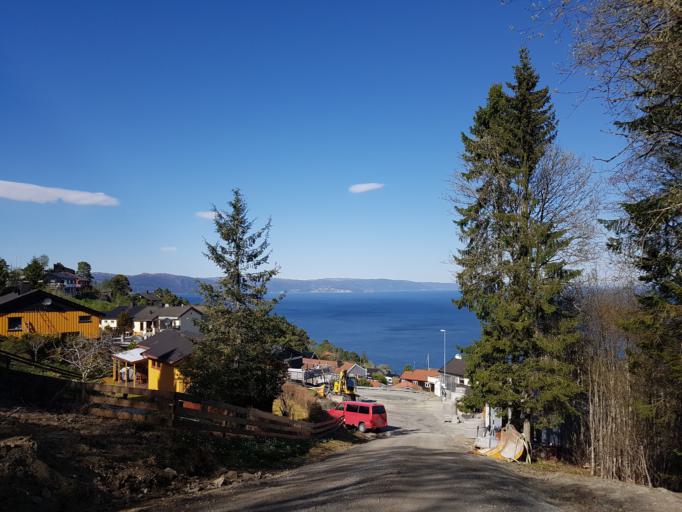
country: NO
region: Sor-Trondelag
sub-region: Trondheim
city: Trondheim
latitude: 63.4487
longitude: 10.3023
